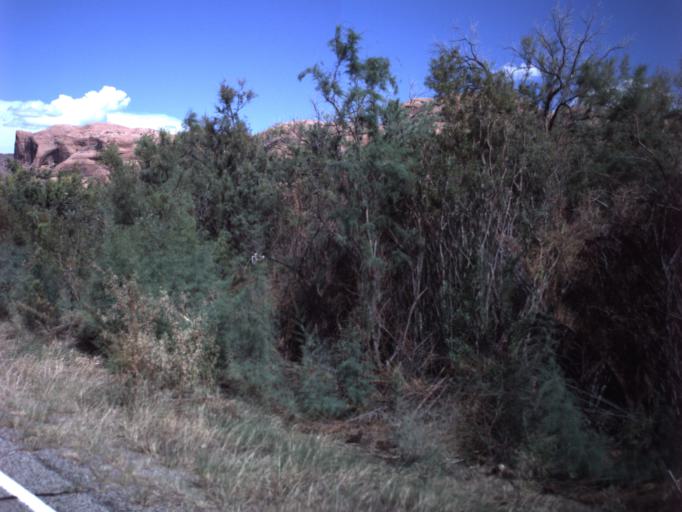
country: US
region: Utah
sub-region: Grand County
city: Moab
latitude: 38.5414
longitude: -109.6014
